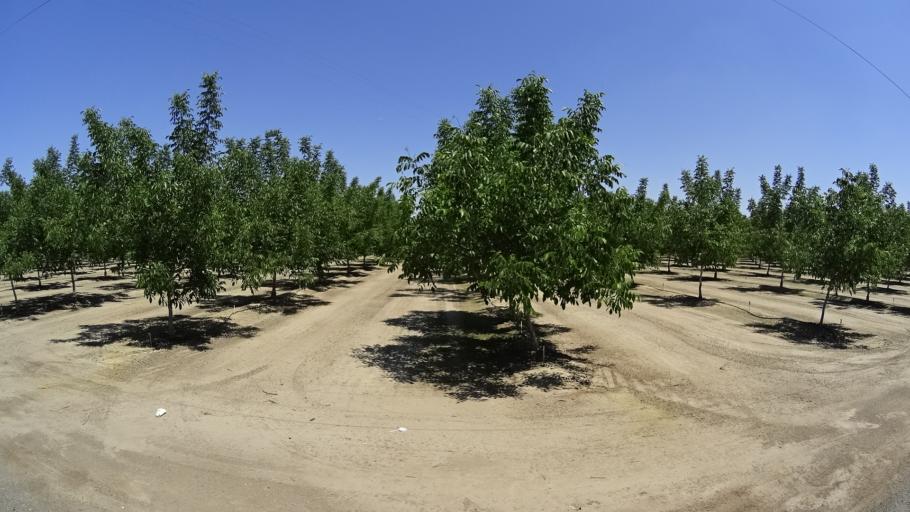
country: US
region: California
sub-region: Kings County
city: Lucerne
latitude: 36.3961
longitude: -119.6550
